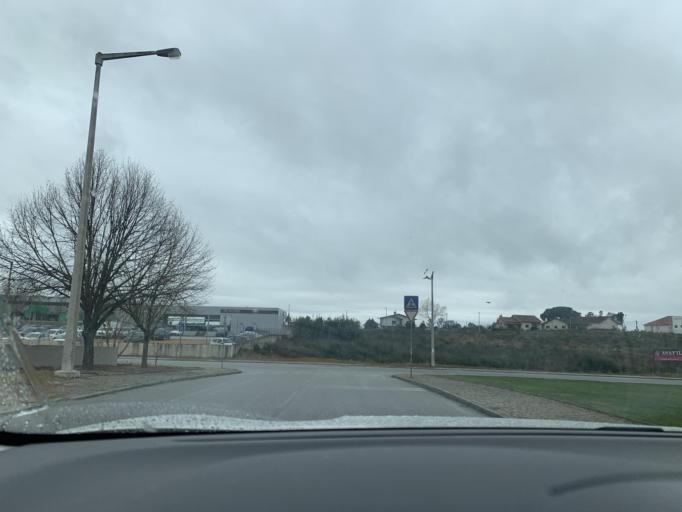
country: PT
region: Viseu
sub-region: Viseu
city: Rio de Loba
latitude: 40.6294
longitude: -7.8748
